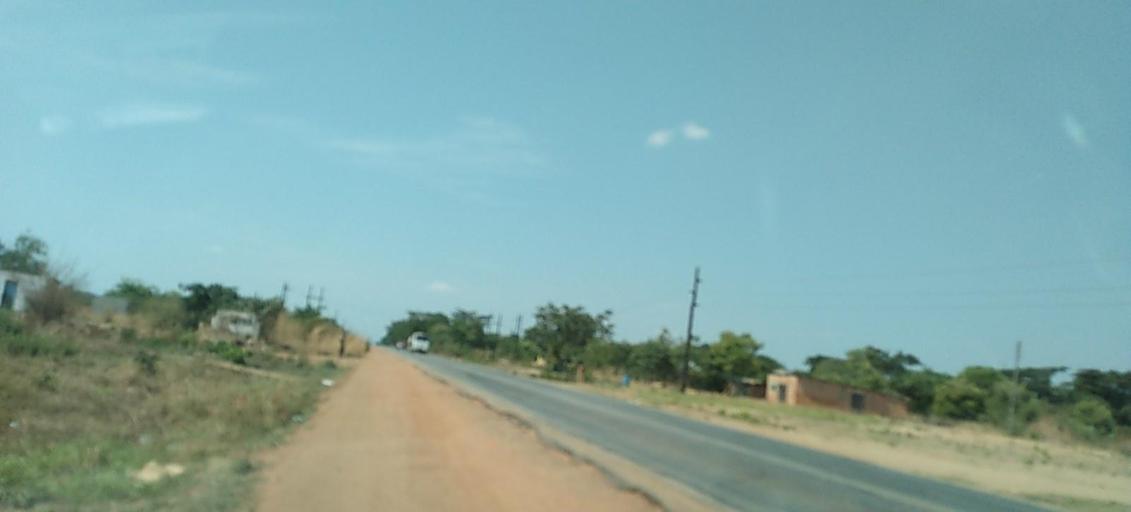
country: ZM
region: Copperbelt
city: Luanshya
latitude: -13.4713
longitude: 28.6729
